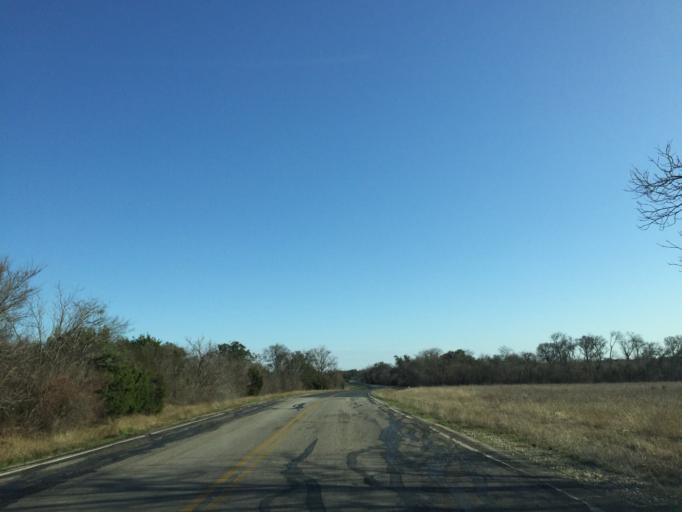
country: US
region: Texas
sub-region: Williamson County
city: Florence
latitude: 30.7796
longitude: -97.7922
